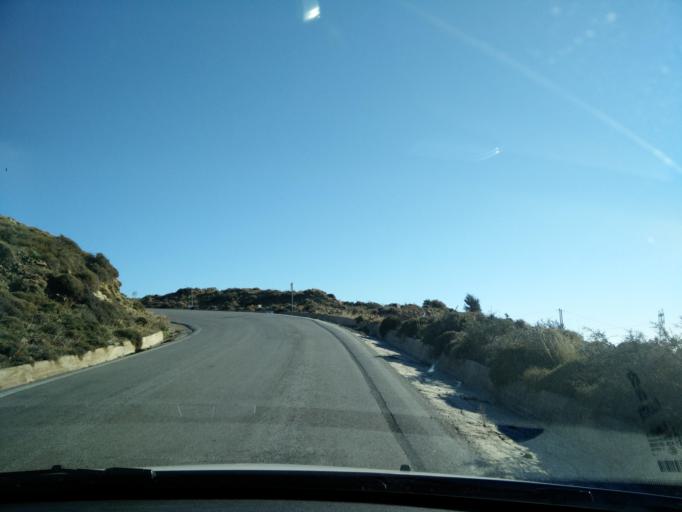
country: GR
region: Crete
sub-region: Nomos Irakleiou
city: Kastelli
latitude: 35.0449
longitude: 25.4229
